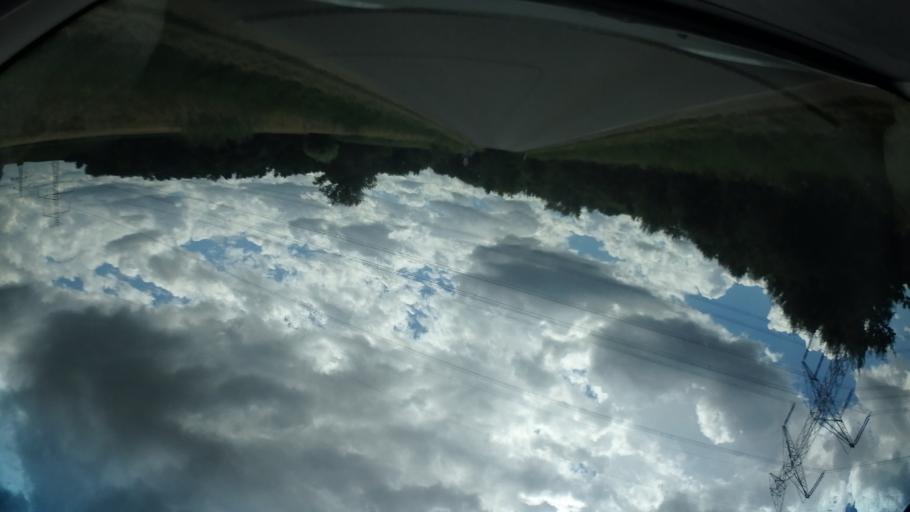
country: CZ
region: South Moravian
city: Orechov
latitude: 49.0616
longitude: 16.5188
